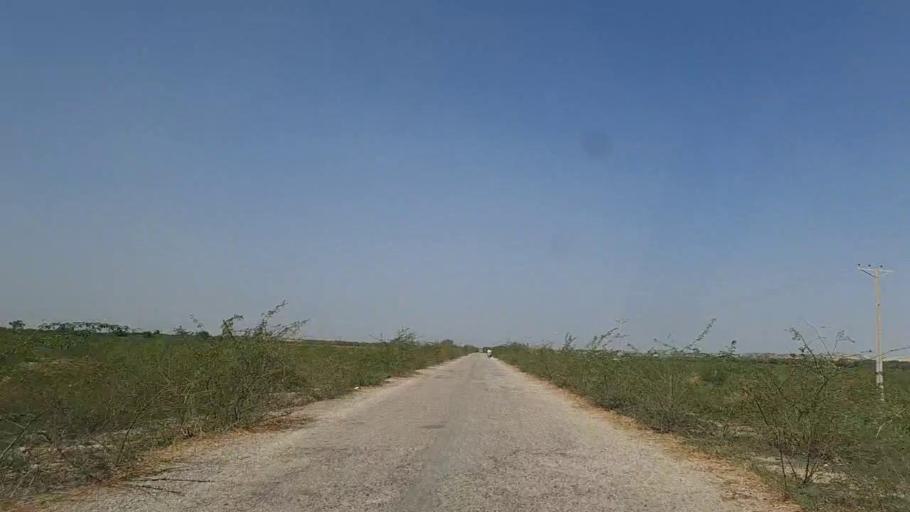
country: PK
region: Sindh
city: Naukot
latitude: 24.6435
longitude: 69.2879
